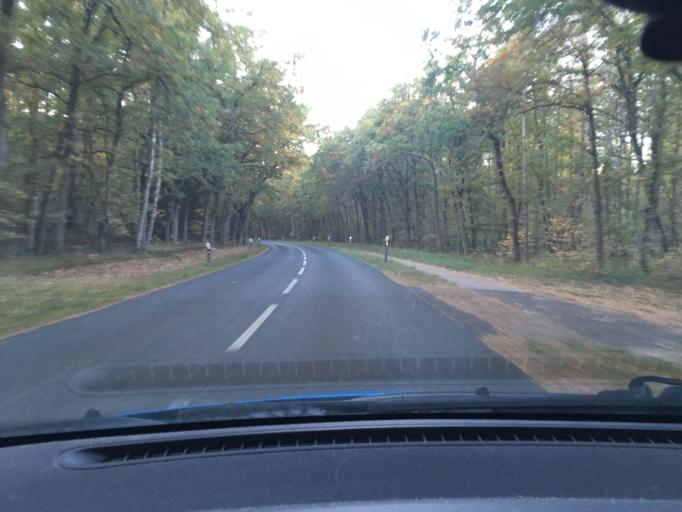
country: DE
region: Lower Saxony
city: Bleckede
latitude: 53.2754
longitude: 10.7768
